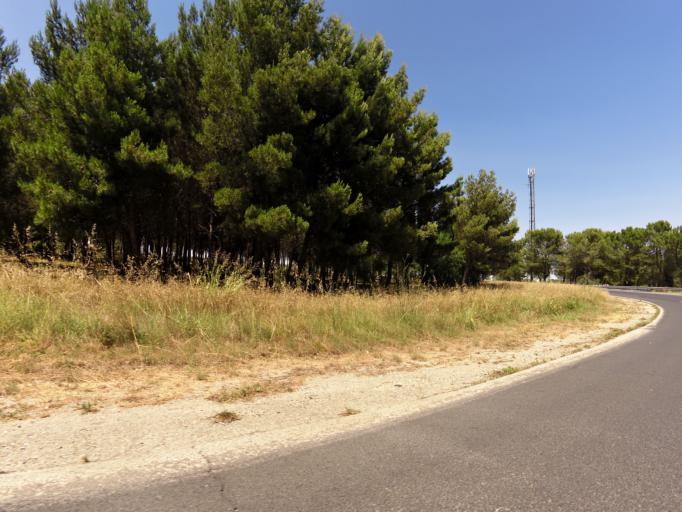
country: FR
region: Languedoc-Roussillon
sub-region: Departement du Gard
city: Aigues-Vives
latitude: 43.7267
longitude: 4.1802
